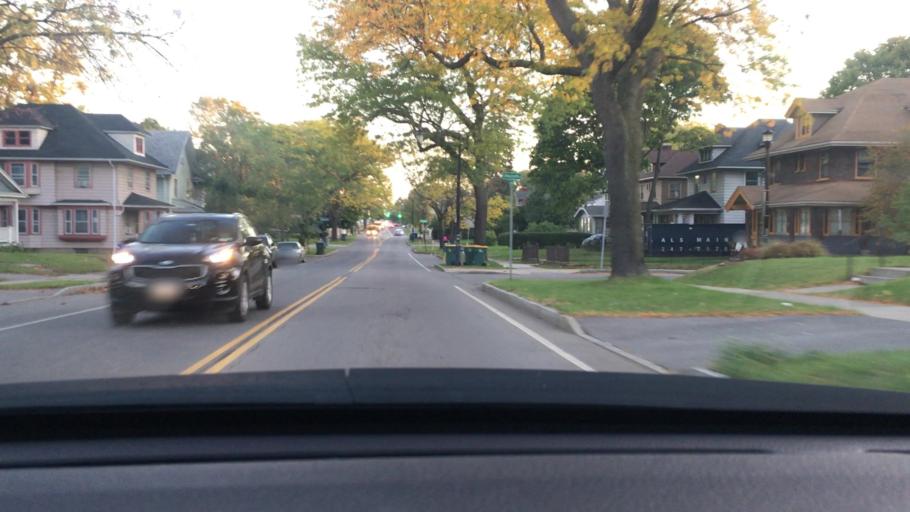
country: US
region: New York
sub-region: Monroe County
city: Brighton
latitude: 43.1620
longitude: -77.5651
